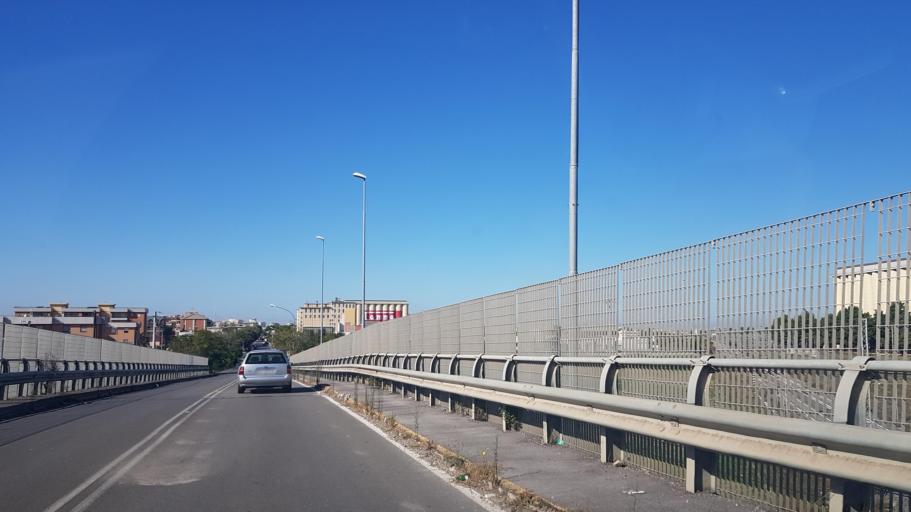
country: IT
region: Apulia
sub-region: Provincia di Foggia
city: Foggia
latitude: 41.4440
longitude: 15.5775
